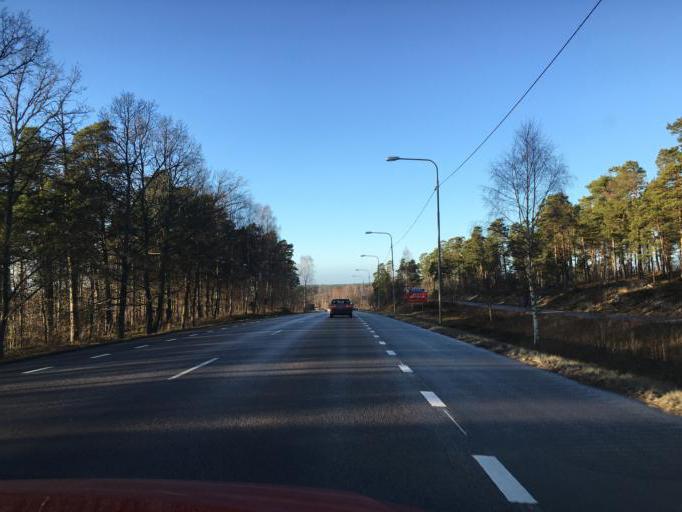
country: SE
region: Kalmar
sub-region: Vasterviks Kommun
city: Vaestervik
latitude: 57.7681
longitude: 16.5841
